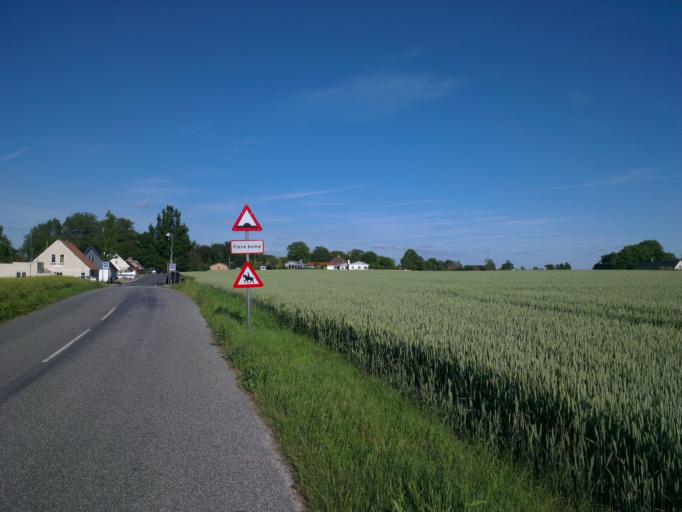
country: DK
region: Capital Region
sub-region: Frederikssund Kommune
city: Skibby
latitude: 55.7379
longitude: 12.0242
